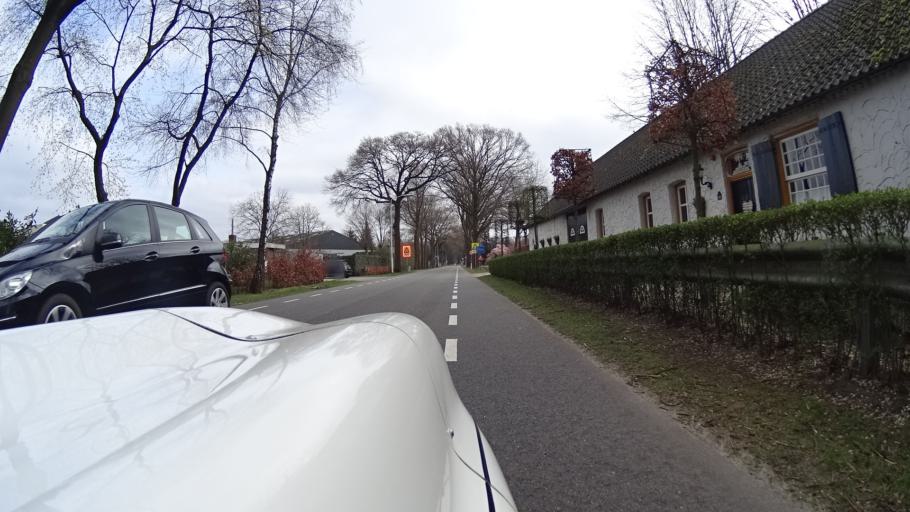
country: NL
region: North Brabant
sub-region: Gemeente Best
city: Best
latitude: 51.5159
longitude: 5.4165
